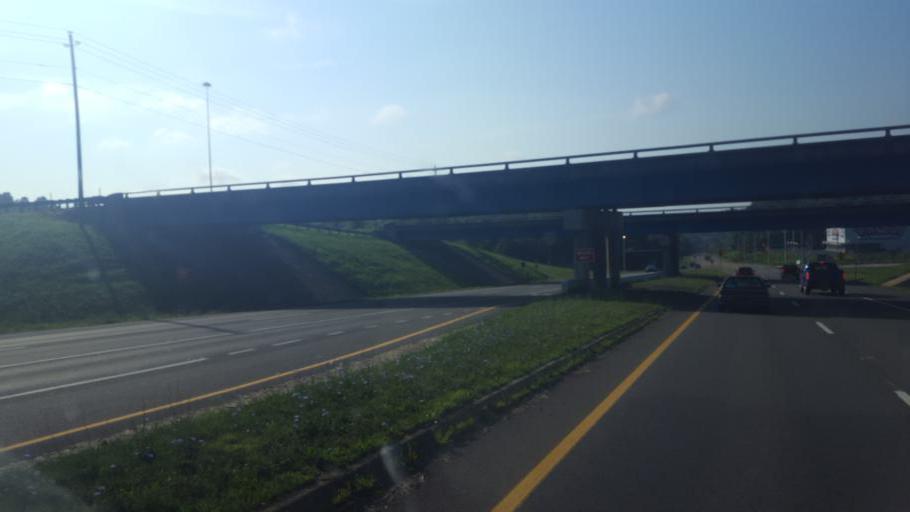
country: US
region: Tennessee
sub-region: Sullivan County
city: Blountville
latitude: 36.5446
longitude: -82.3362
